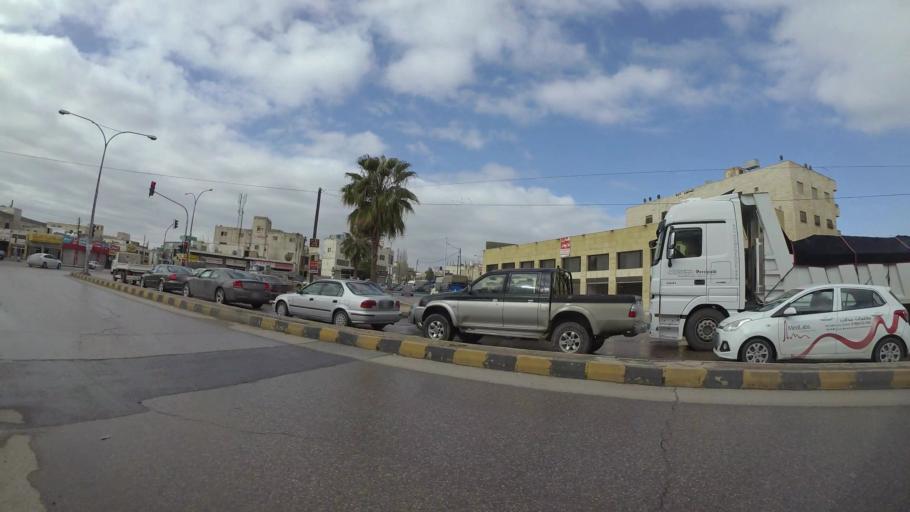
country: JO
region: Amman
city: Wadi as Sir
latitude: 31.9463
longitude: 35.8399
